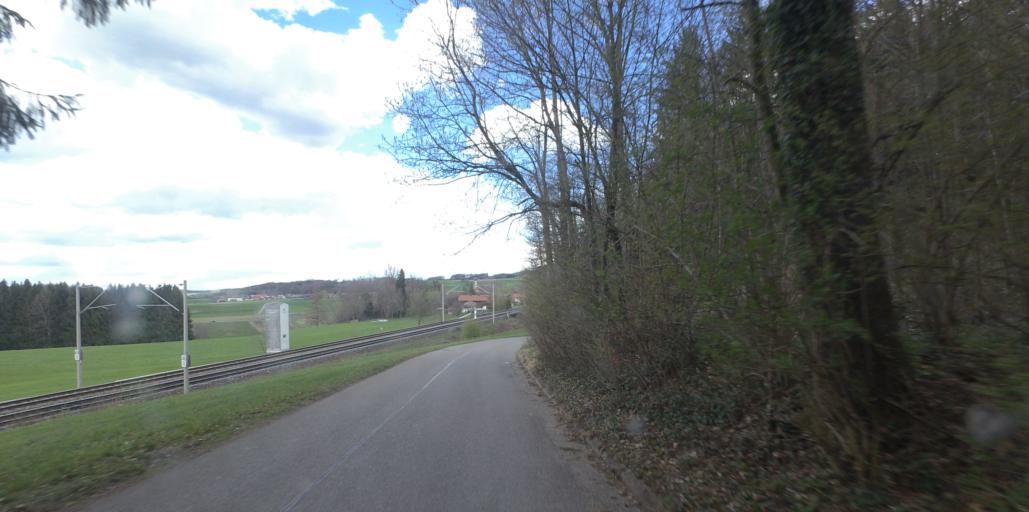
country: DE
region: Bavaria
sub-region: Upper Bavaria
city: Vachendorf
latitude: 47.8337
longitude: 12.6038
